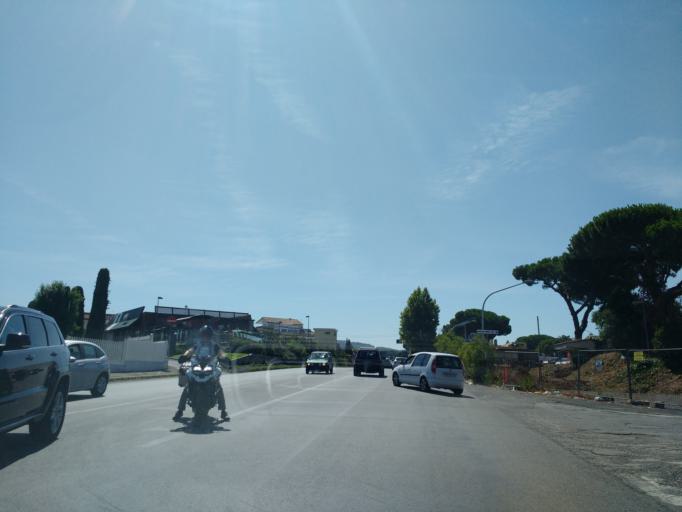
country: IT
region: Latium
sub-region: Citta metropolitana di Roma Capitale
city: Marino
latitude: 41.7681
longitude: 12.6152
